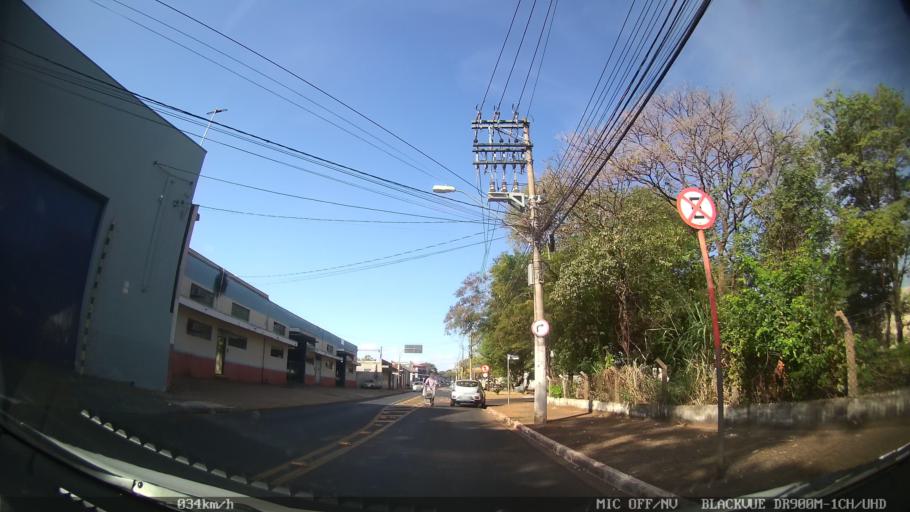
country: BR
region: Sao Paulo
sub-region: Ribeirao Preto
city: Ribeirao Preto
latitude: -21.1841
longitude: -47.7617
